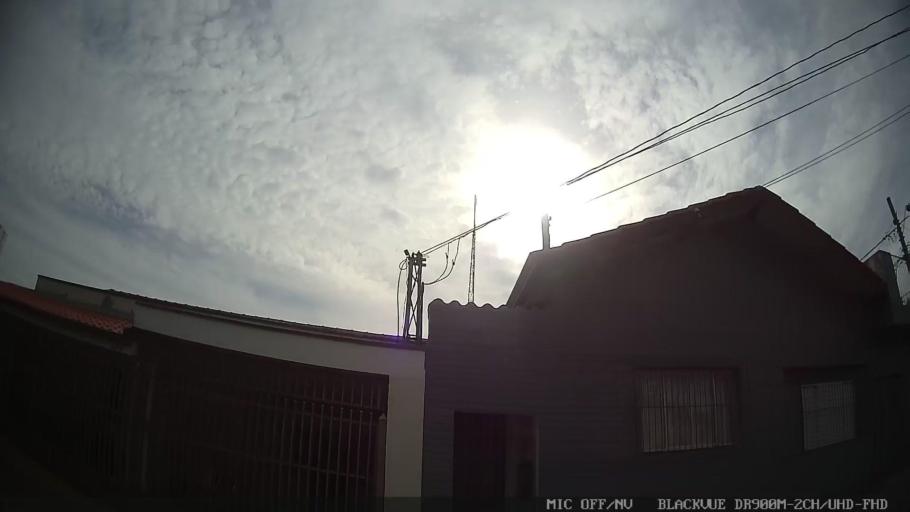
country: BR
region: Sao Paulo
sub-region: Indaiatuba
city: Indaiatuba
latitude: -23.0852
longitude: -47.2191
